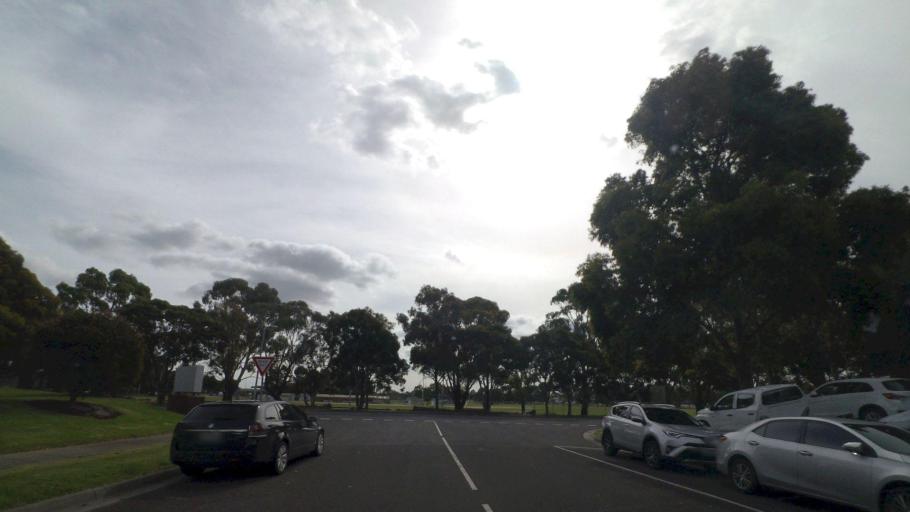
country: AU
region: Victoria
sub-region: Knox
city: Knoxfield
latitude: -37.8959
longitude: 145.2534
